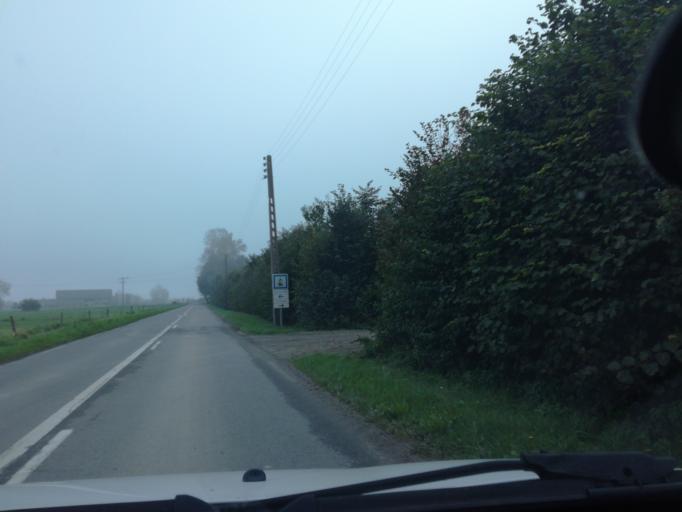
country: FR
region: Brittany
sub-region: Departement d'Ille-et-Vilaine
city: Cherrueix
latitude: 48.6032
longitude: -1.7160
